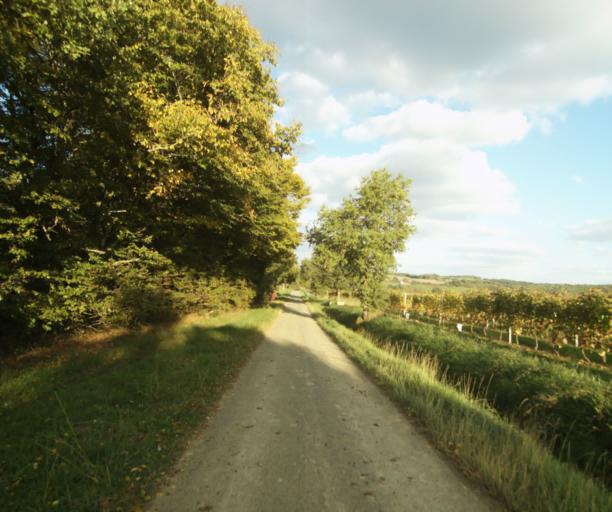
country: FR
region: Midi-Pyrenees
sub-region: Departement du Gers
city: Eauze
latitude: 43.7567
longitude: 0.1533
